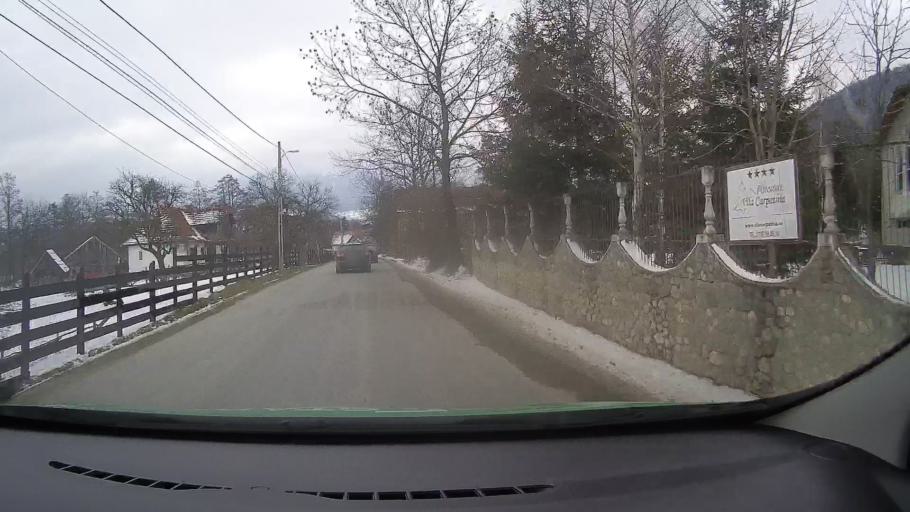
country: RO
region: Brasov
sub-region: Comuna Bran
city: Bran
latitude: 45.5251
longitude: 25.3643
